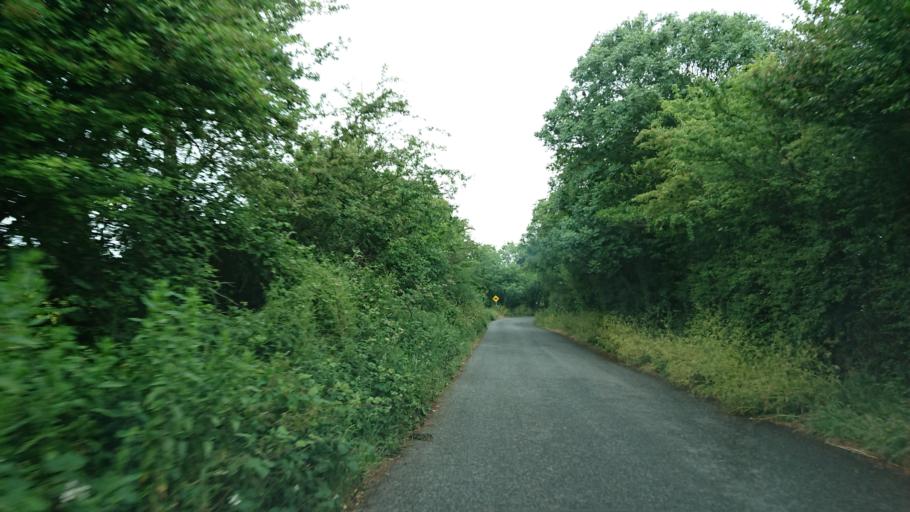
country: IE
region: Munster
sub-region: Waterford
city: Waterford
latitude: 52.2260
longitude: -7.1469
